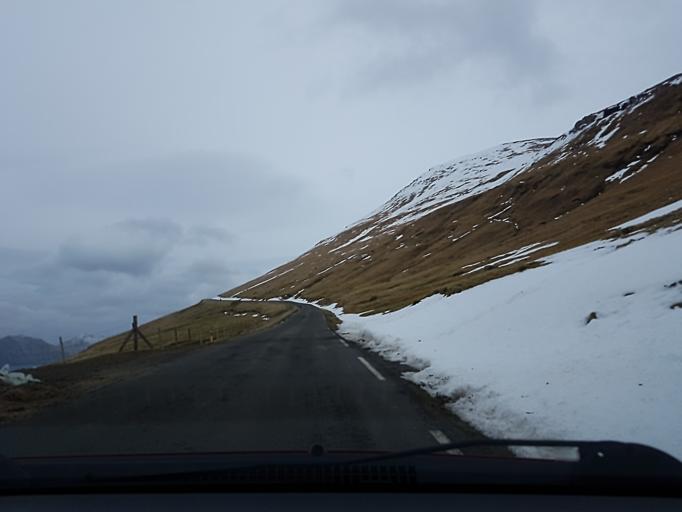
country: FO
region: Streymoy
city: Kollafjordhur
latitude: 61.9993
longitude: -6.8979
